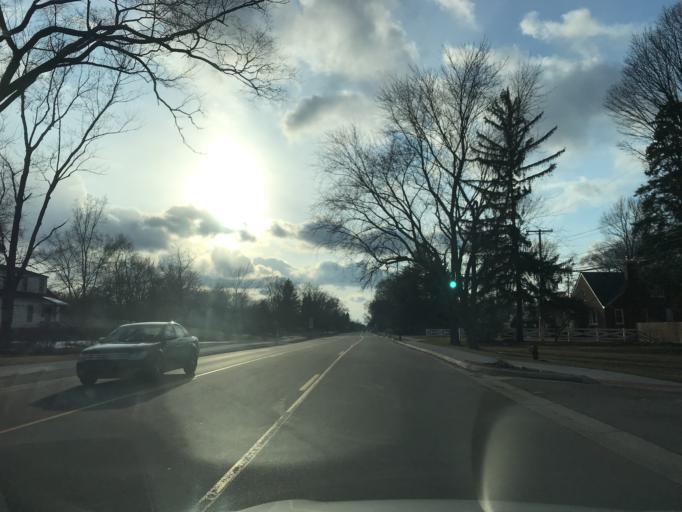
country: US
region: Michigan
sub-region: Oakland County
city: Bingham Farms
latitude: 42.4574
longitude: -83.2815
